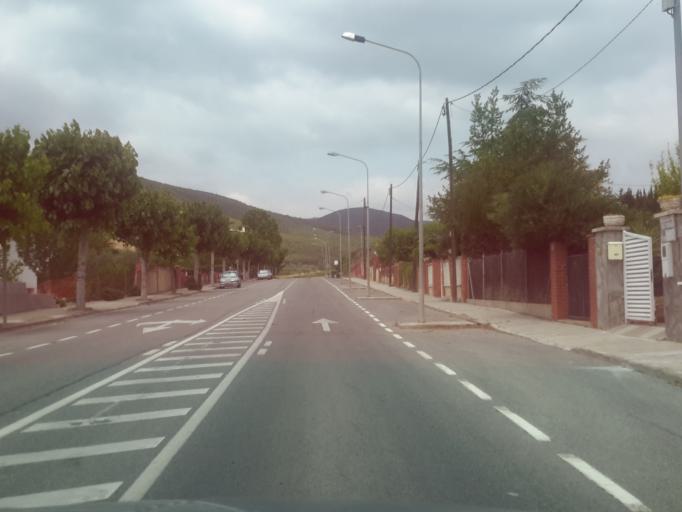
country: ES
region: Catalonia
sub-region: Provincia de Barcelona
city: Sant Marti Sarroca
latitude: 41.3901
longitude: 1.5667
